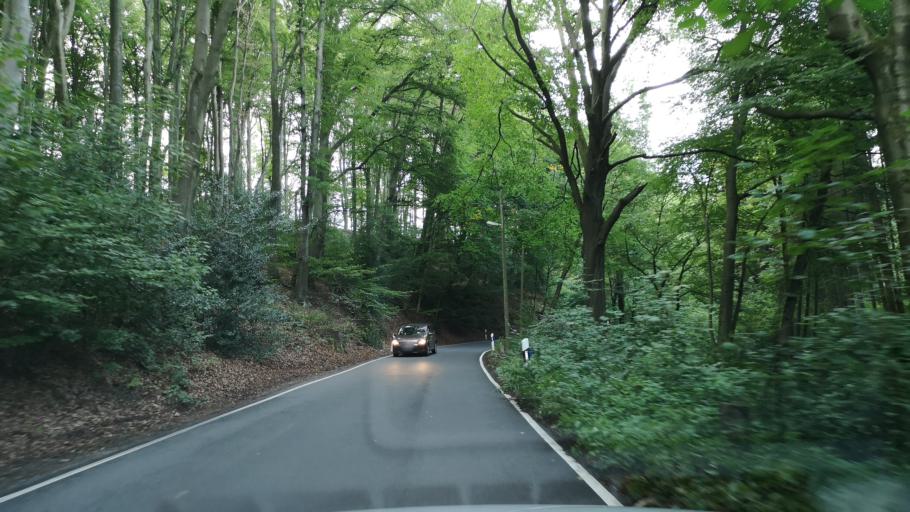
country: DE
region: North Rhine-Westphalia
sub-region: Regierungsbezirk Dusseldorf
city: Velbert
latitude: 51.3870
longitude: 7.1032
